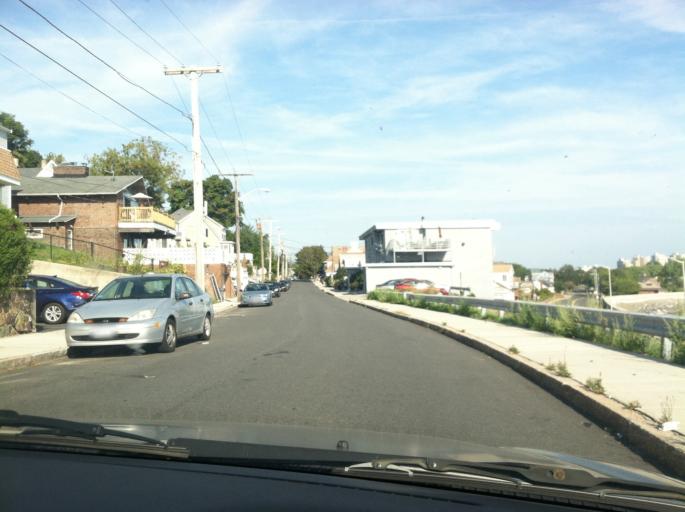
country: US
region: Massachusetts
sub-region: Suffolk County
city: Winthrop
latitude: 42.3954
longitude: -70.9829
